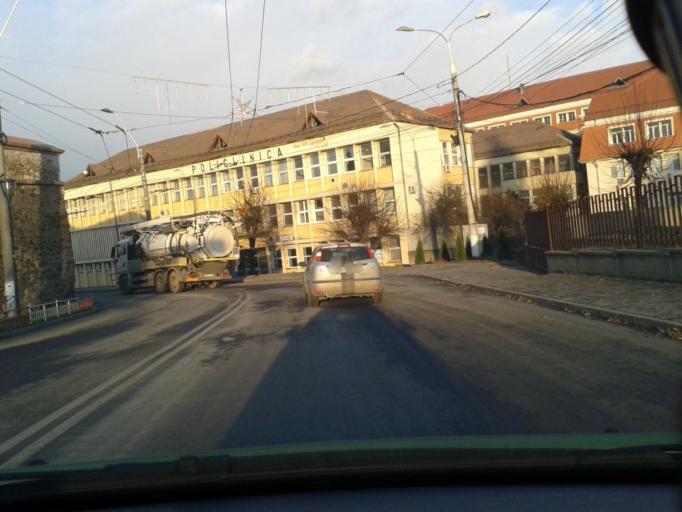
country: RO
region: Sibiu
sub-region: Municipiul Medias
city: Medias
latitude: 46.1626
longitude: 24.3559
